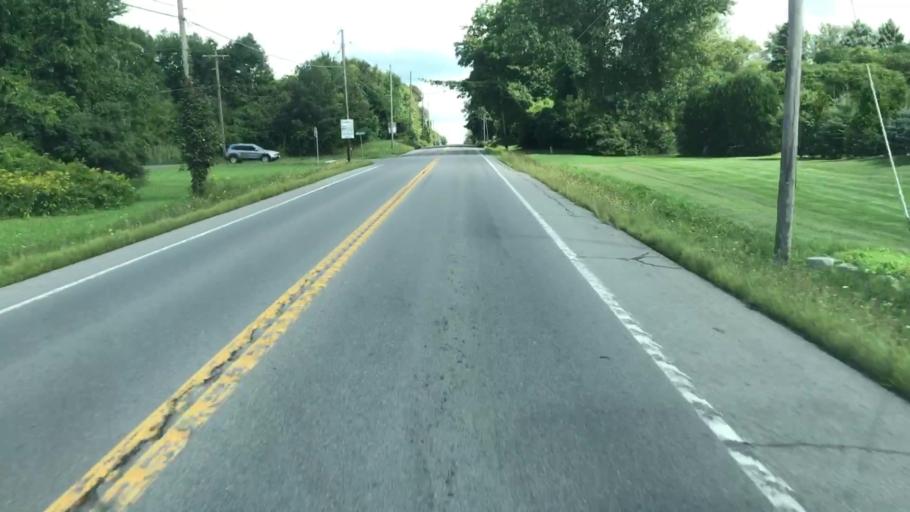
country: US
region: New York
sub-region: Onondaga County
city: Marcellus
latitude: 42.9838
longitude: -76.3090
